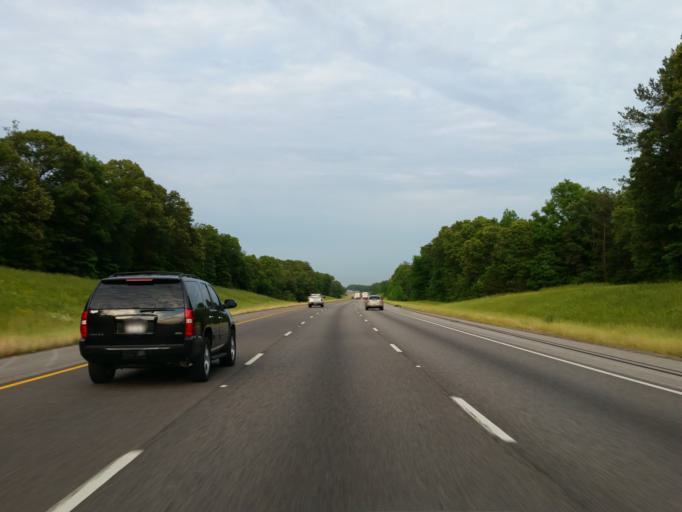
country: US
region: Alabama
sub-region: Calhoun County
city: Bynum
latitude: 33.5801
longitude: -85.9662
